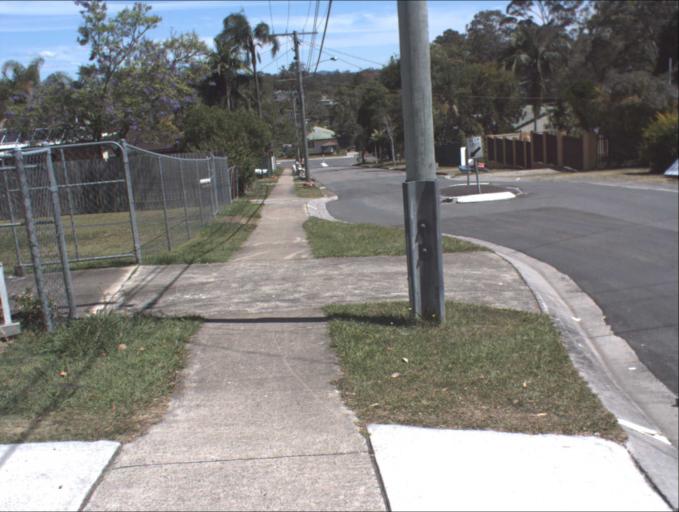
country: AU
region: Queensland
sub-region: Logan
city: Logan City
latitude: -27.6486
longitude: 153.1244
